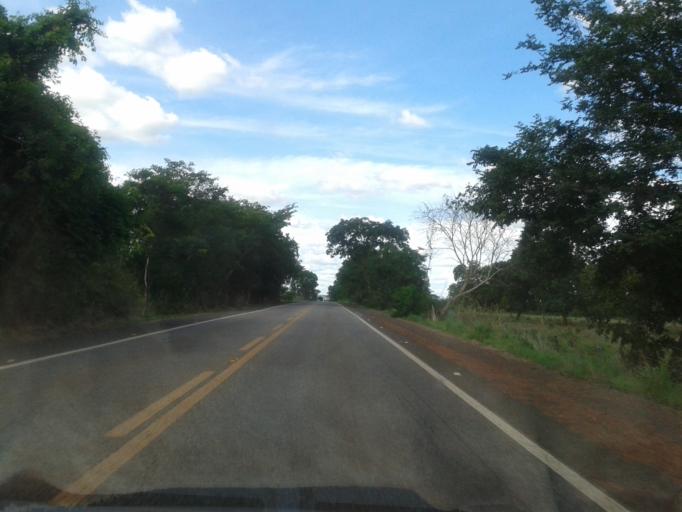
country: BR
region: Goias
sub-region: Mozarlandia
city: Mozarlandia
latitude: -15.0311
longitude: -50.6012
